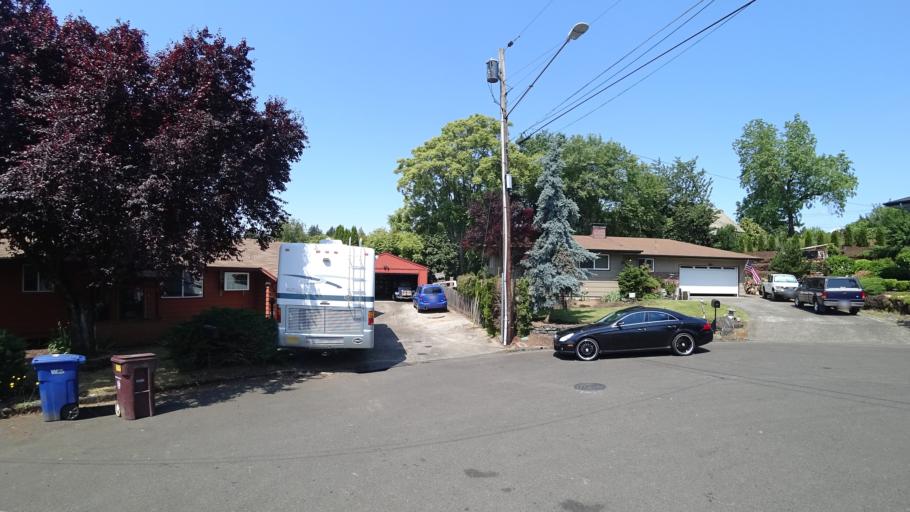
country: US
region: Oregon
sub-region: Clackamas County
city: Oatfield
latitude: 45.4460
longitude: -122.5878
